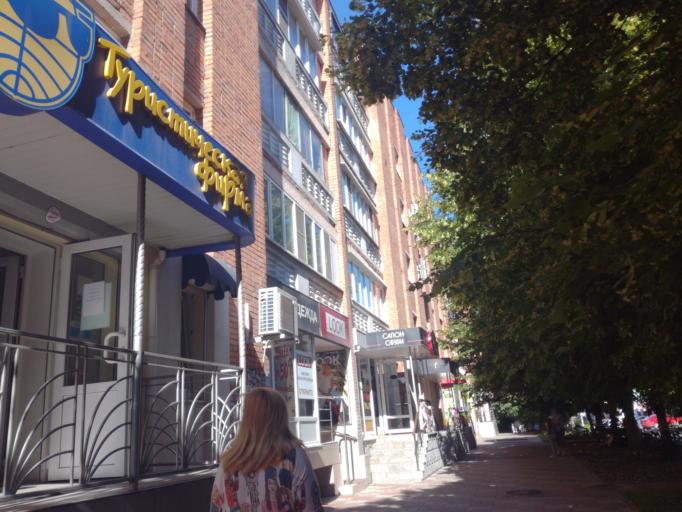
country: RU
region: Kursk
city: Kursk
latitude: 51.7462
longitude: 36.1910
